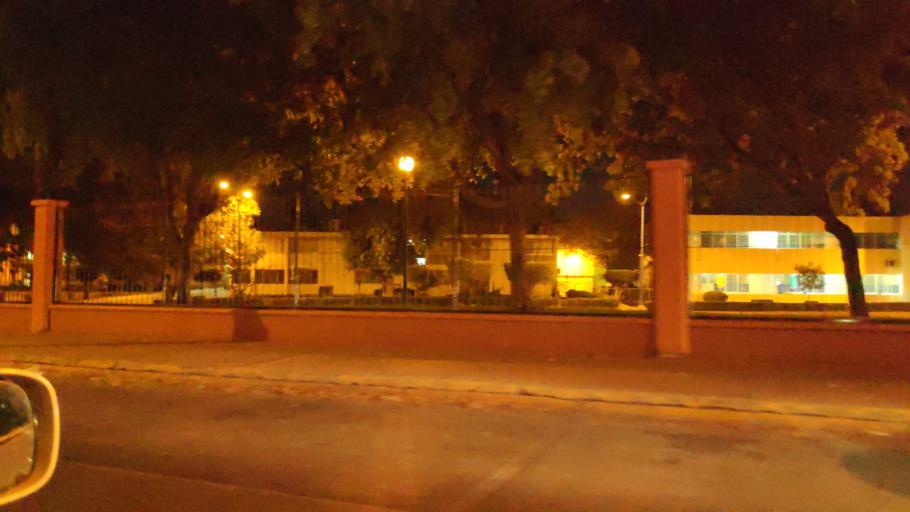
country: MX
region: Sinaloa
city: Culiacan
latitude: 24.8292
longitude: -107.3820
